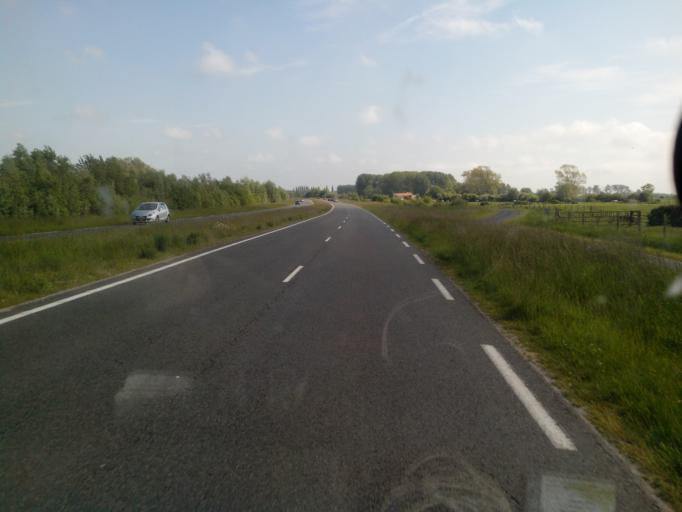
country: FR
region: Picardie
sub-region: Departement de la Somme
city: Rue
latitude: 50.2905
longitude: 1.6512
